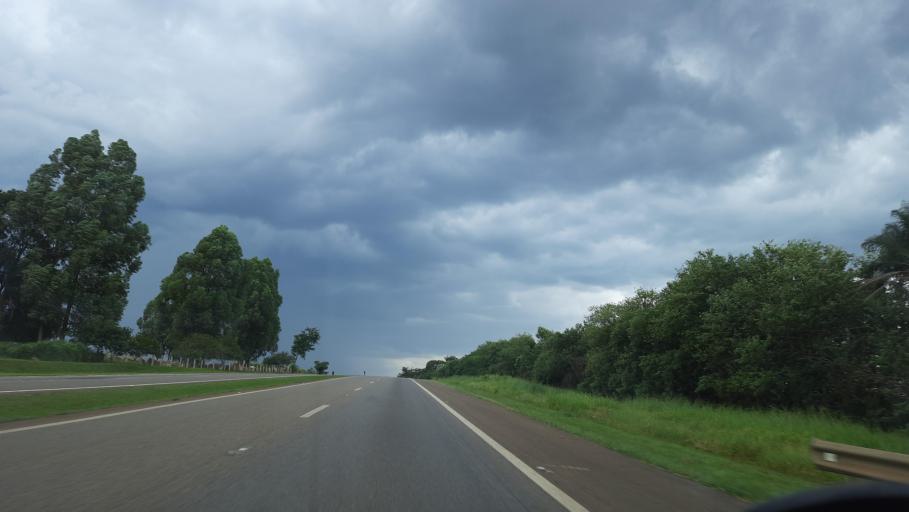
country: BR
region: Sao Paulo
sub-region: Aguai
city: Aguai
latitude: -22.0536
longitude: -47.0292
